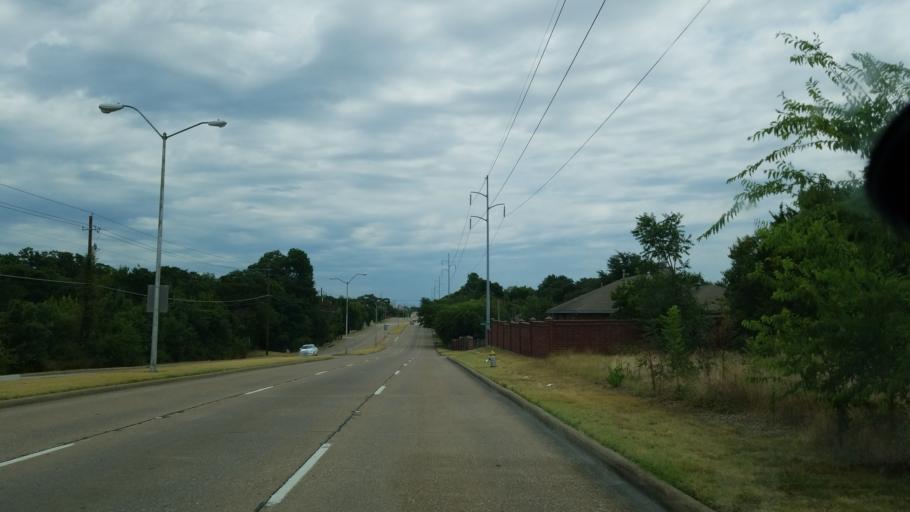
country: US
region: Texas
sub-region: Dallas County
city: Duncanville
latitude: 32.6620
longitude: -96.8544
